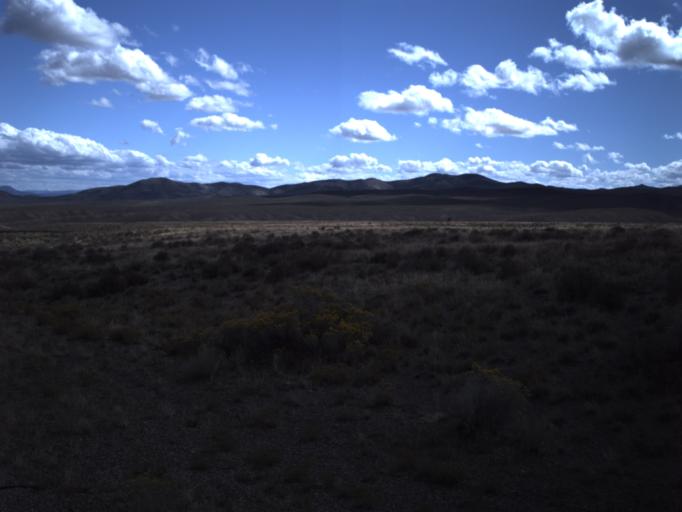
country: US
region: Utah
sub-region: Beaver County
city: Milford
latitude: 38.4454
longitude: -113.1812
